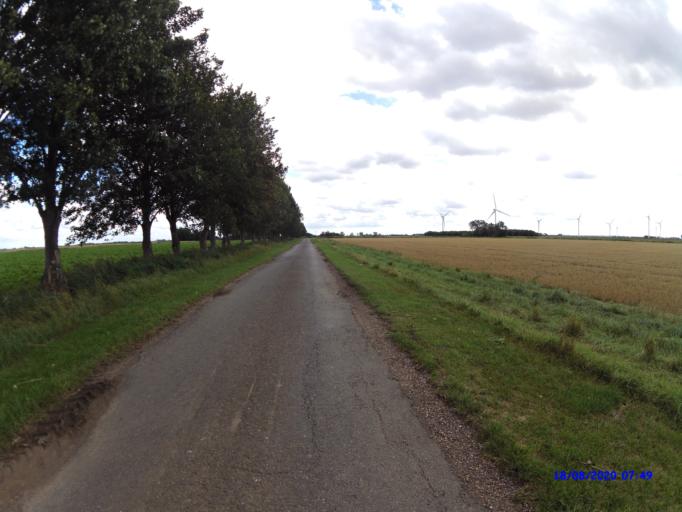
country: GB
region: England
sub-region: Cambridgeshire
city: Whittlesey
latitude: 52.5207
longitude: -0.0954
